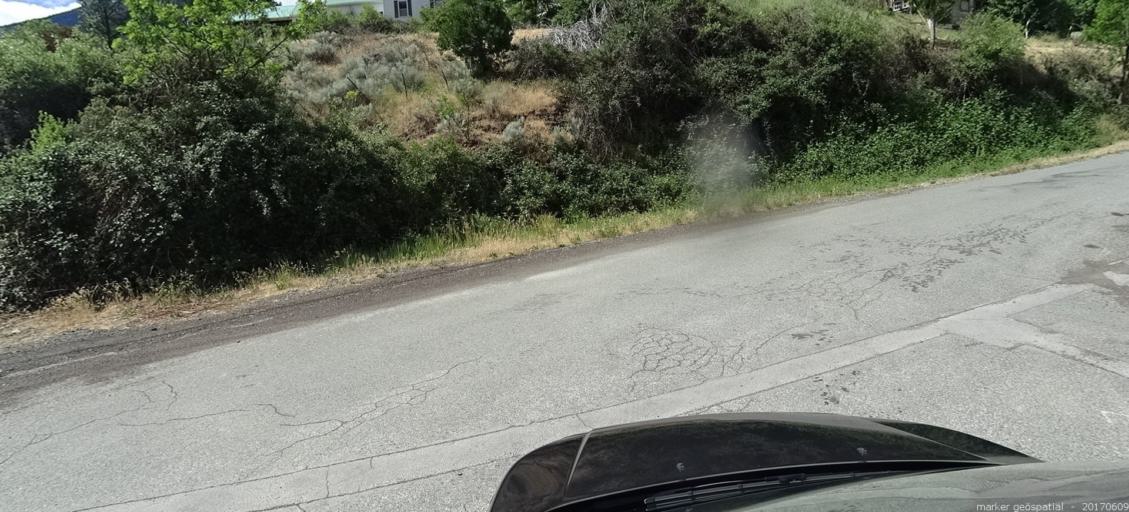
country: US
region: California
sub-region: Siskiyou County
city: Weed
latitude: 41.3089
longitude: -122.8000
